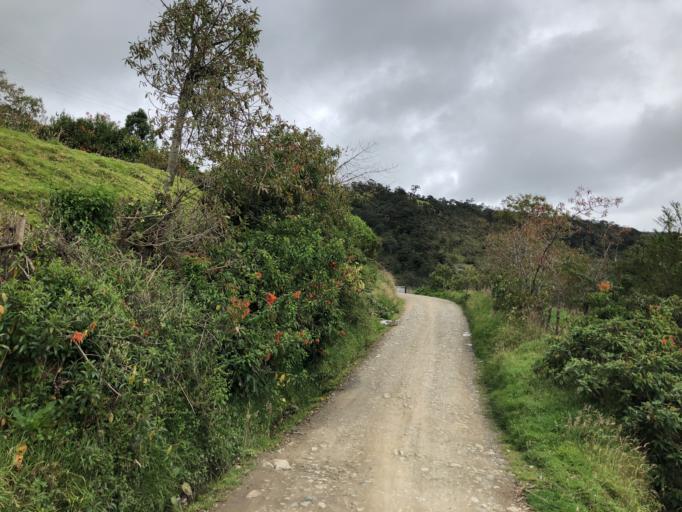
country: CO
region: Cauca
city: Totoro
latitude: 2.5029
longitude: -76.3592
